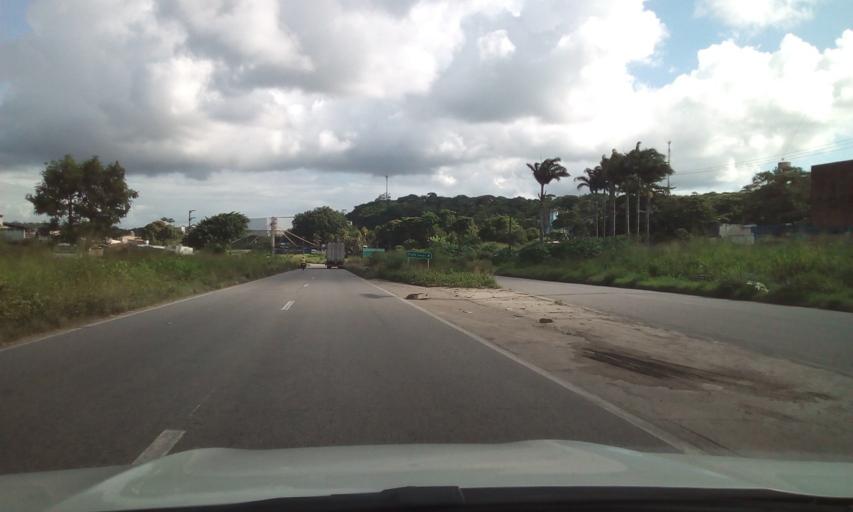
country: BR
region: Pernambuco
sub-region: Abreu E Lima
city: Abreu e Lima
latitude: -7.9307
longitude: -34.9004
